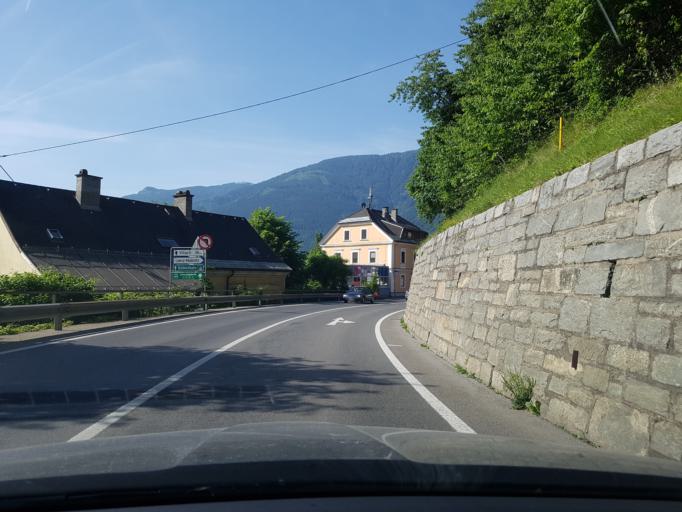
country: AT
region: Carinthia
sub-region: Politischer Bezirk Spittal an der Drau
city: Spittal an der Drau
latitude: 46.8010
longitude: 13.4980
